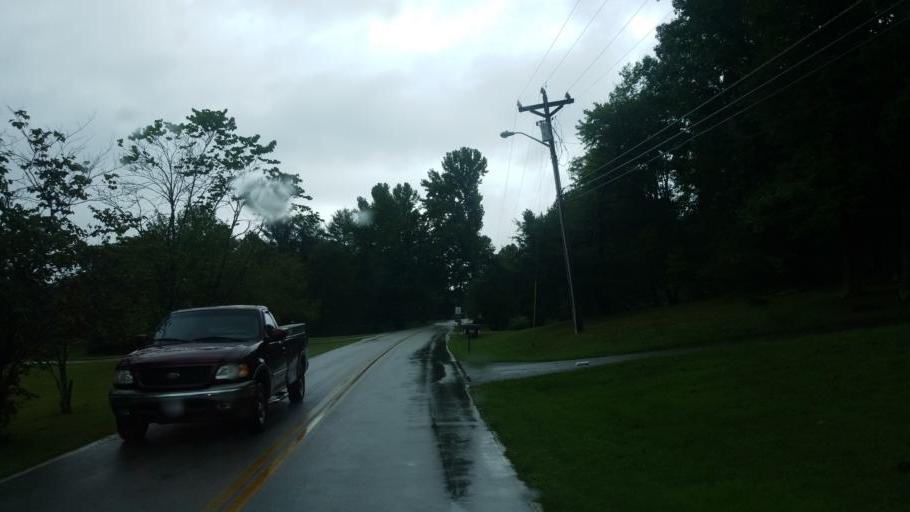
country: US
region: Kentucky
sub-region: Rowan County
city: Morehead
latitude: 38.1817
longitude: -83.4827
